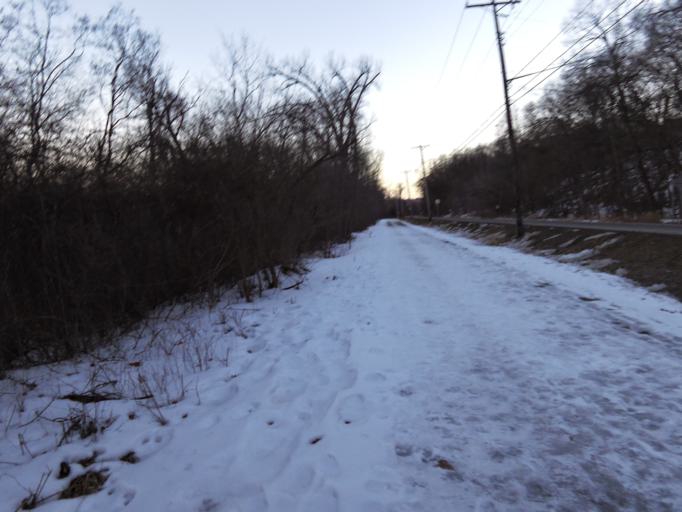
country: US
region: Minnesota
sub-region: Washington County
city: Stillwater
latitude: 45.0693
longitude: -92.8061
